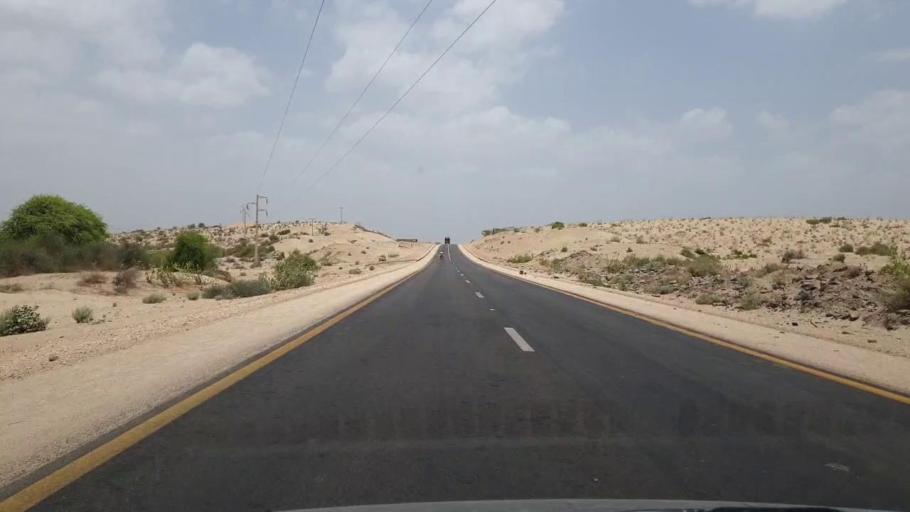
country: PK
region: Sindh
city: Naukot
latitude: 24.8386
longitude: 69.4625
